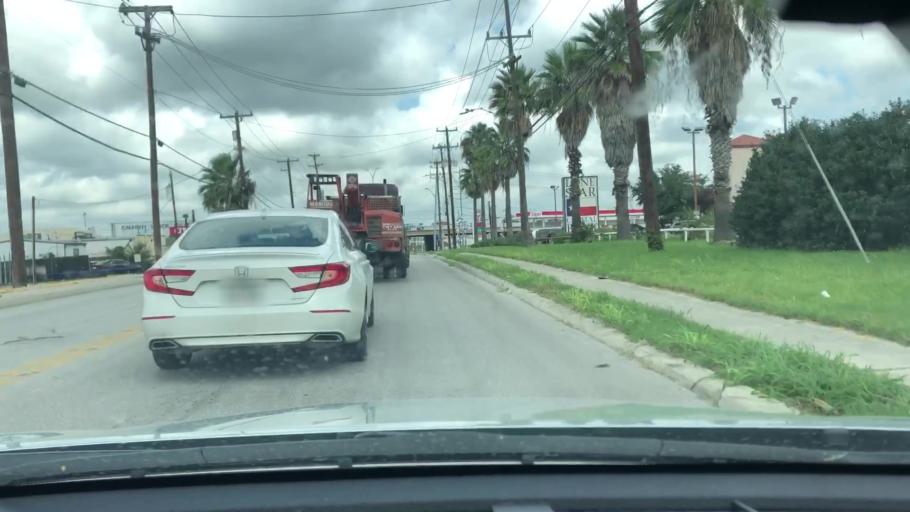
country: US
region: Texas
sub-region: Bexar County
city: Windcrest
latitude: 29.5380
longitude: -98.3792
